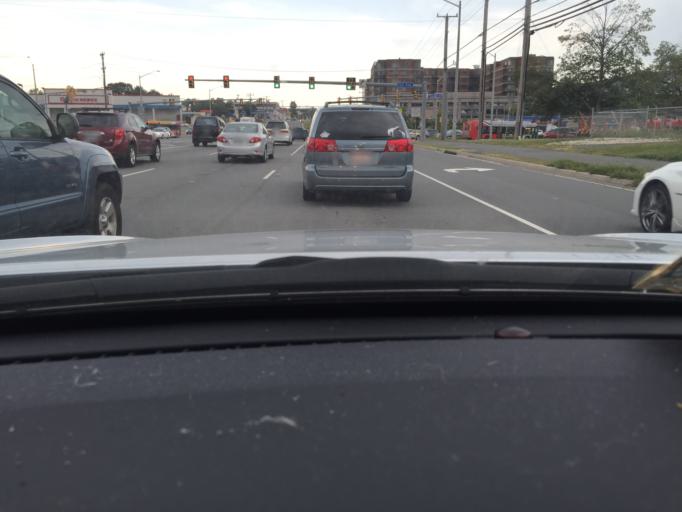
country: US
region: Virginia
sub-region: Fairfax County
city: Merrifield
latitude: 38.8755
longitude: -77.2271
